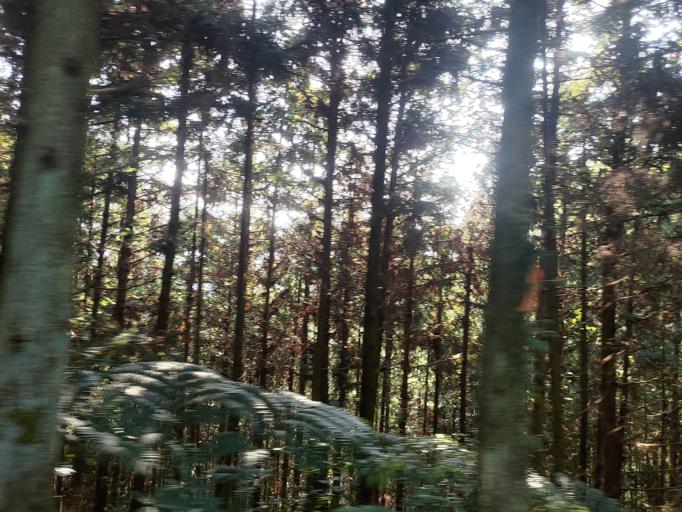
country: TW
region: Taiwan
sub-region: Hsinchu
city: Hsinchu
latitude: 24.6223
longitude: 121.0906
